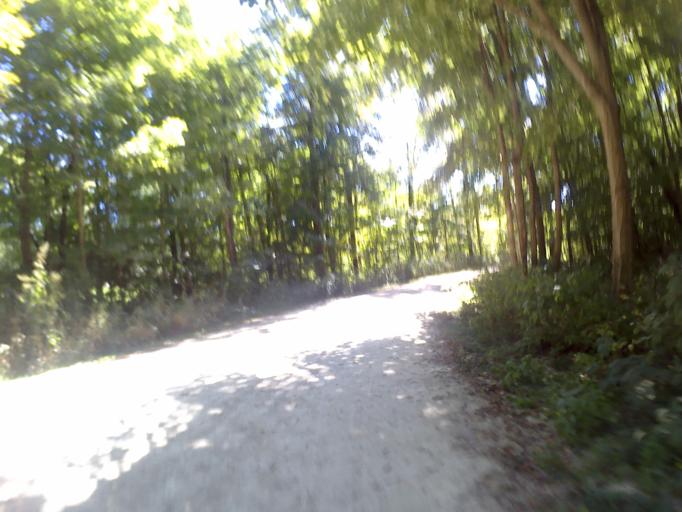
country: US
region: Illinois
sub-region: DuPage County
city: Naperville
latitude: 41.7872
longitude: -88.1773
